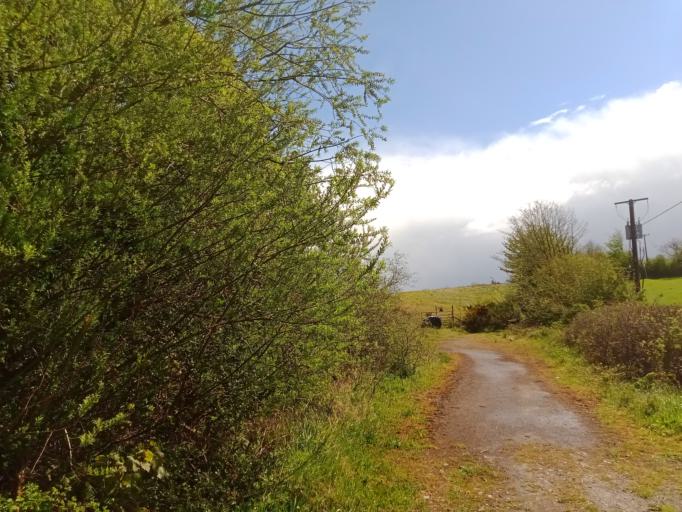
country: IE
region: Leinster
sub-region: Kilkenny
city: Kilkenny
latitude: 52.6935
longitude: -7.2683
